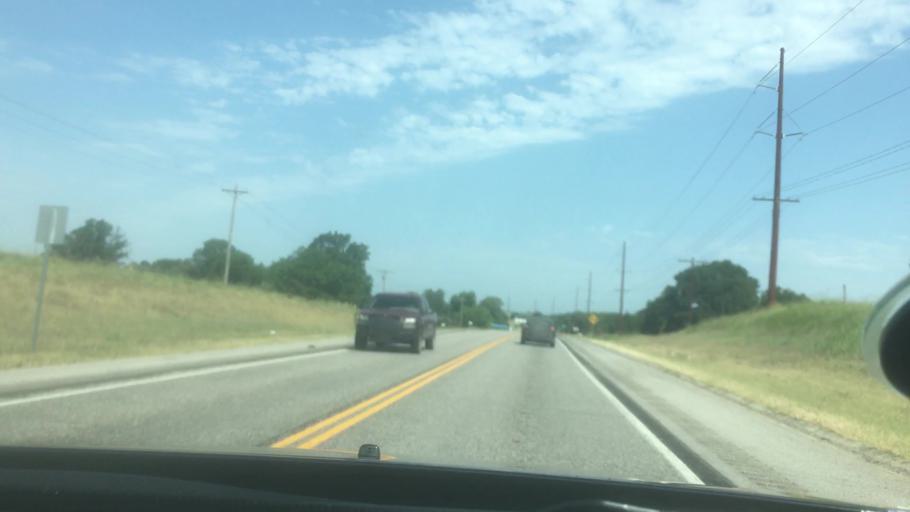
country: US
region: Oklahoma
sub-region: Seminole County
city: Konawa
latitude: 34.8588
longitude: -96.8216
